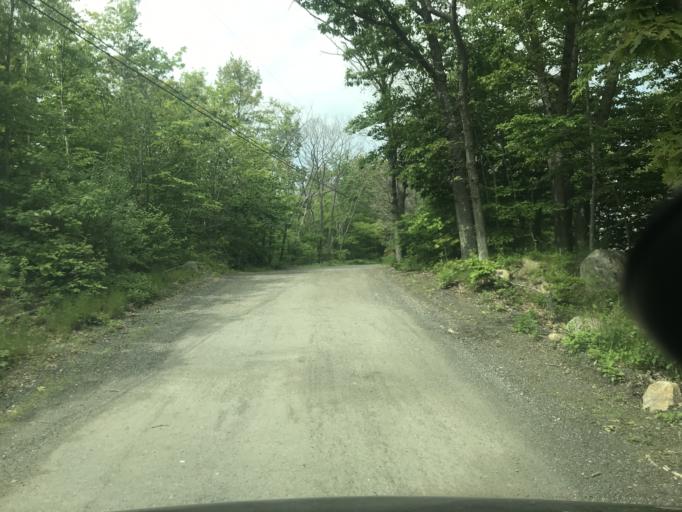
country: US
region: Massachusetts
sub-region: Essex County
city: Rockport
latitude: 42.6595
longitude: -70.6369
